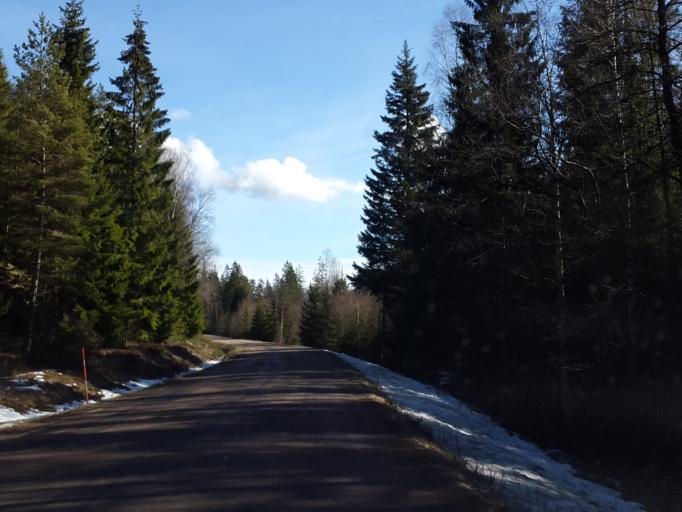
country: SE
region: Vaestra Goetaland
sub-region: Boras Kommun
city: Sjomarken
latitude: 57.8283
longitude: 12.8350
